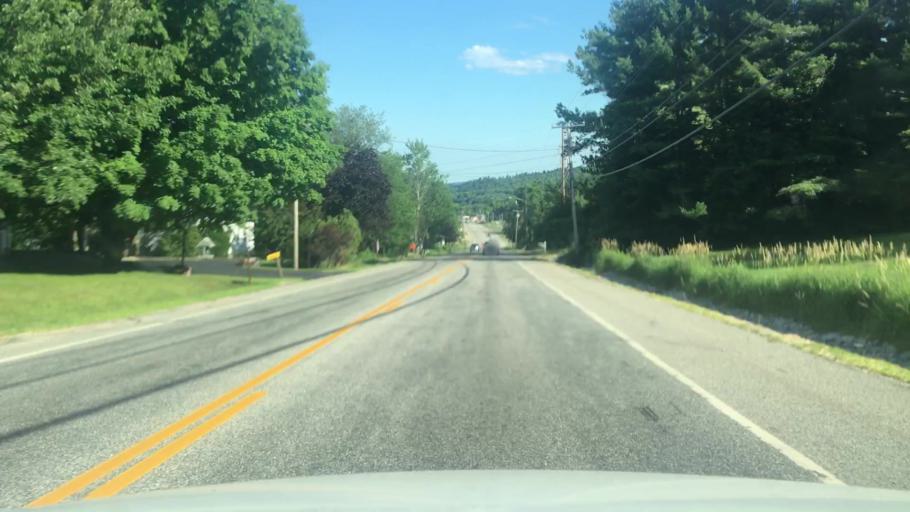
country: US
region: Maine
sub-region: Franklin County
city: Jay
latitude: 44.5119
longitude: -70.2214
